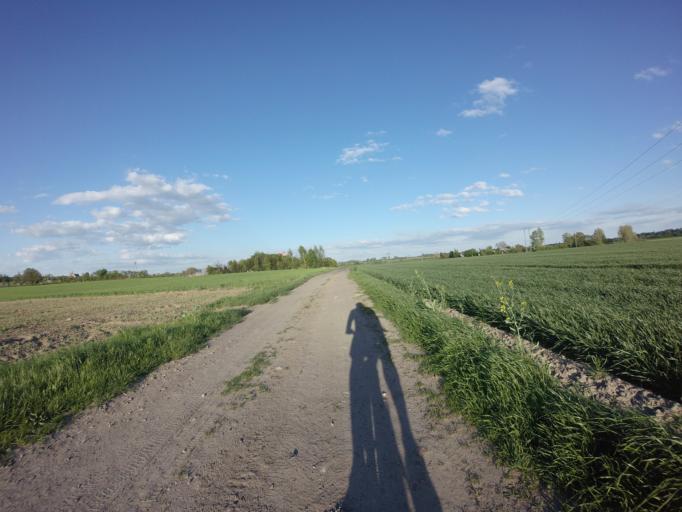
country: PL
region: West Pomeranian Voivodeship
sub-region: Powiat choszczenski
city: Choszczno
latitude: 53.1435
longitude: 15.4278
